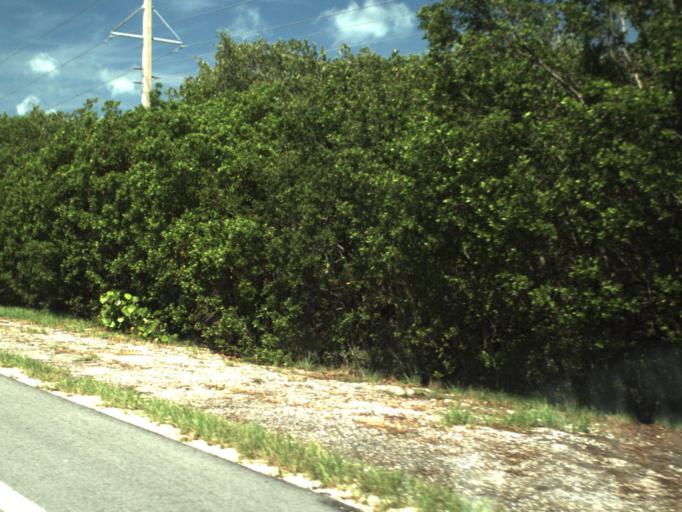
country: US
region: Florida
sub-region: Monroe County
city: Marathon
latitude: 24.7517
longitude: -80.9696
